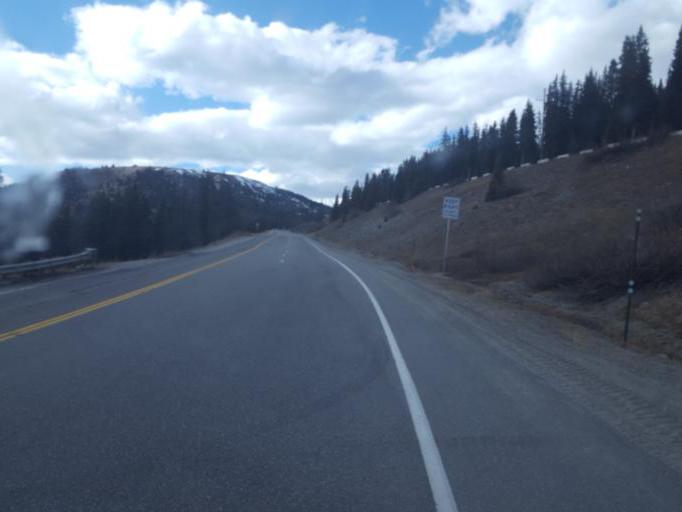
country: US
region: Colorado
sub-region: Lake County
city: Leadville
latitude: 39.3632
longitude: -106.1795
